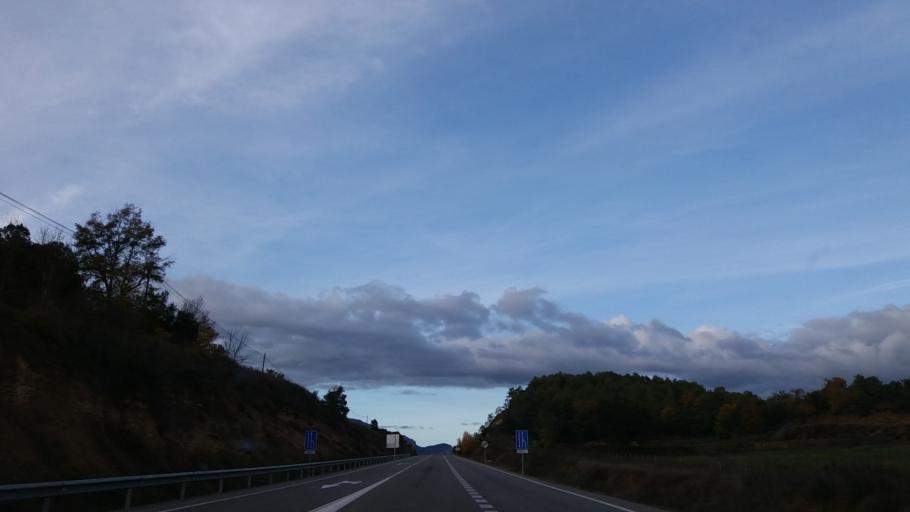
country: ES
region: Catalonia
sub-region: Provincia de Lleida
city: Tiurana
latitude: 42.0159
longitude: 1.2943
